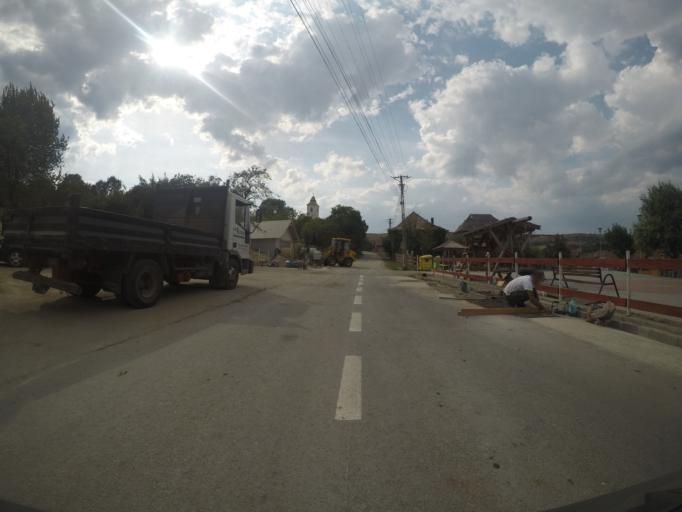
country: RO
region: Cluj
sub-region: Comuna Sandulesti
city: Sandulesti
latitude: 46.5803
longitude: 23.7218
